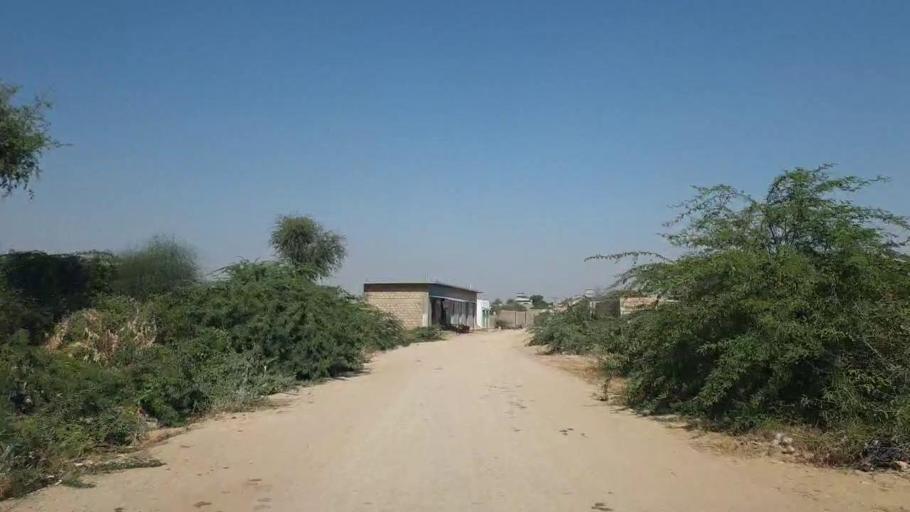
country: PK
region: Sindh
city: Jamshoro
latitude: 25.3557
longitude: 67.8314
